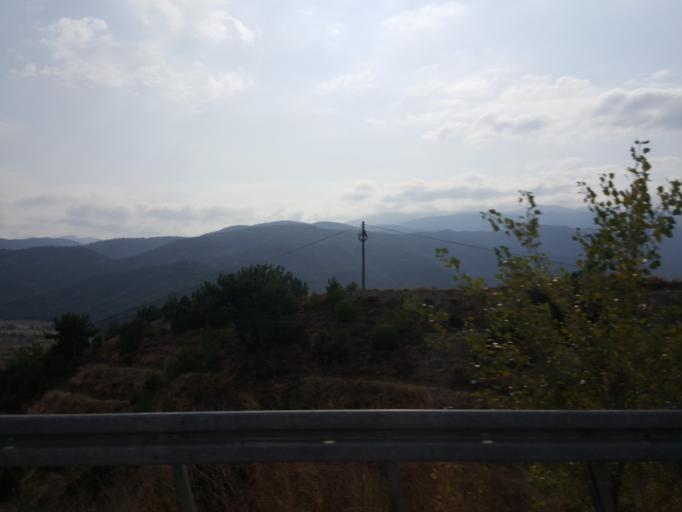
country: TR
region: Corum
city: Hacihamza
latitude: 41.1057
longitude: 34.3776
